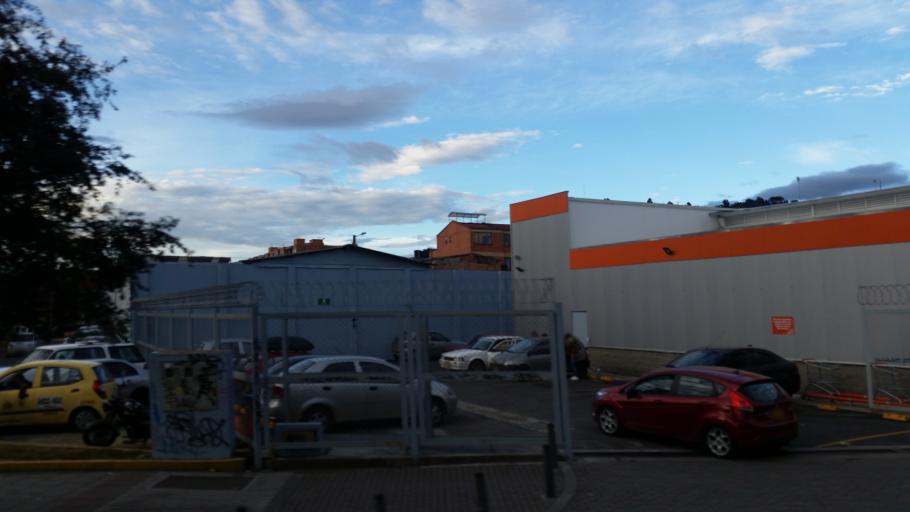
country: CO
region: Cundinamarca
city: Cota
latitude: 4.7404
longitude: -74.0883
